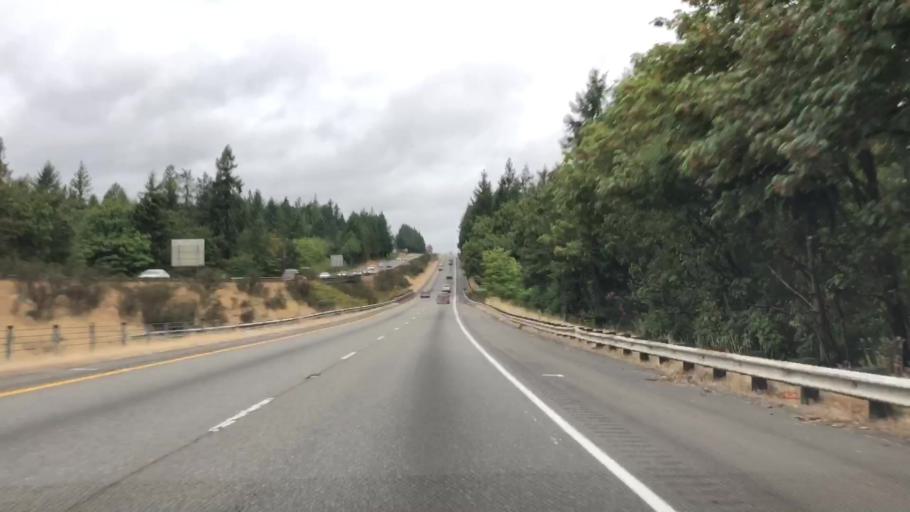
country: US
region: Washington
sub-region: Pierce County
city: Gig Harbor
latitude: 47.3293
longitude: -122.5979
